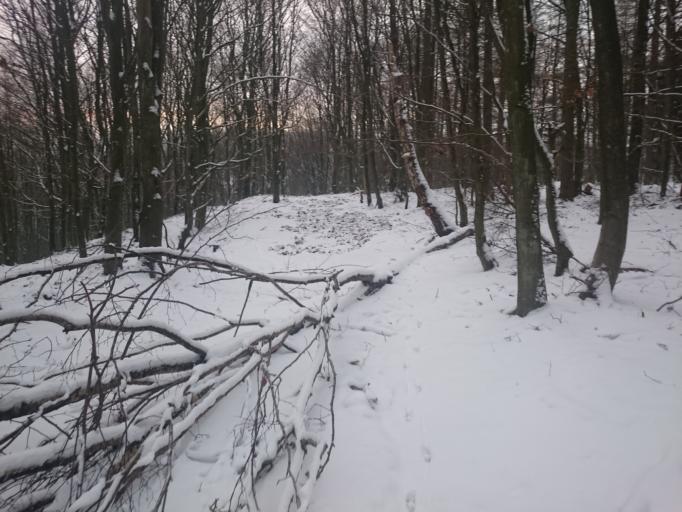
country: SE
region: Skane
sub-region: Sjobo Kommun
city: Sjoebo
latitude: 55.6023
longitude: 13.7615
